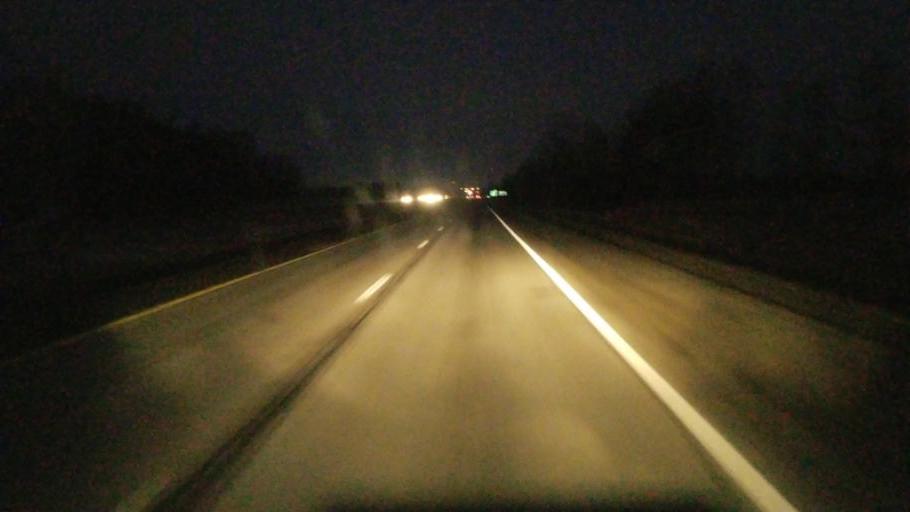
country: US
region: Ohio
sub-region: Preble County
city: Lewisburg
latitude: 39.8378
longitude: -84.5110
